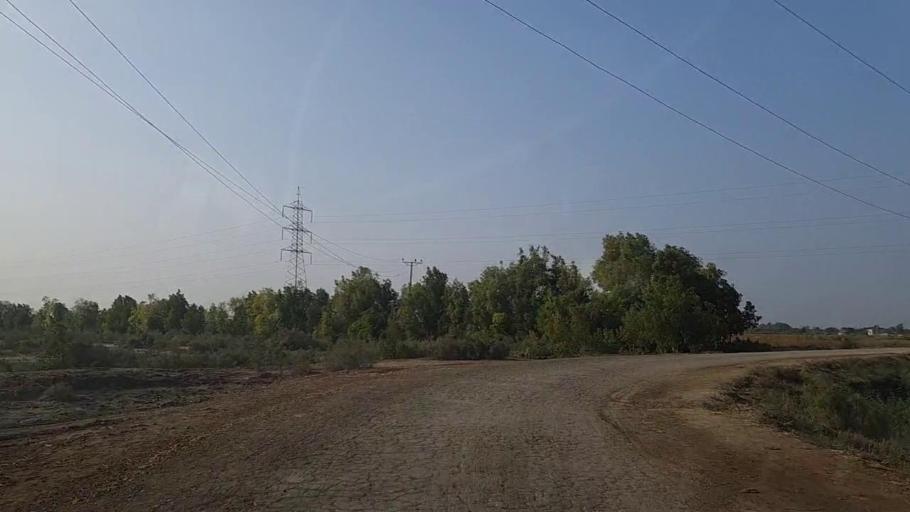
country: PK
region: Sindh
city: Mirpur Sakro
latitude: 24.5632
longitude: 67.6700
